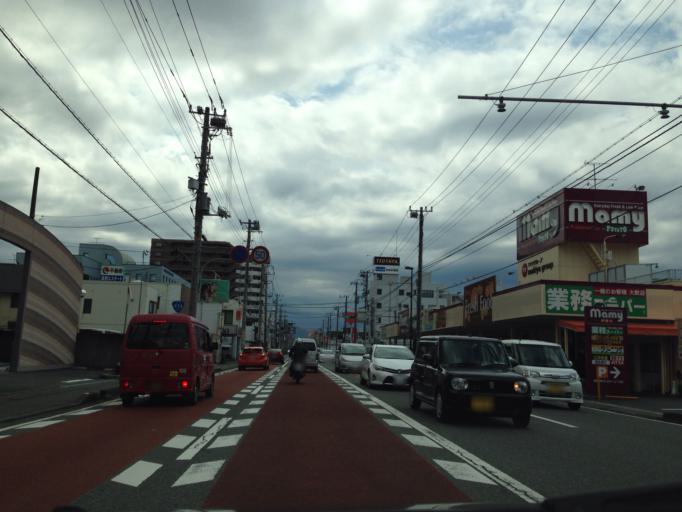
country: JP
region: Shizuoka
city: Numazu
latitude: 35.0903
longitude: 138.8663
